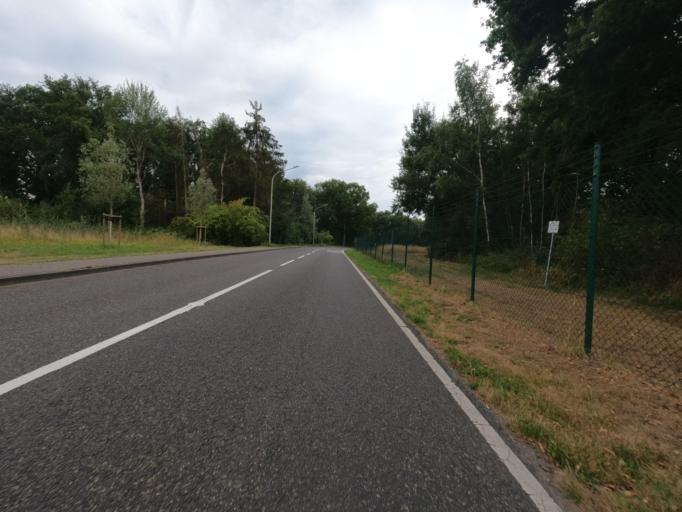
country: DE
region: North Rhine-Westphalia
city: Geilenkirchen
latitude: 50.9809
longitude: 6.1070
